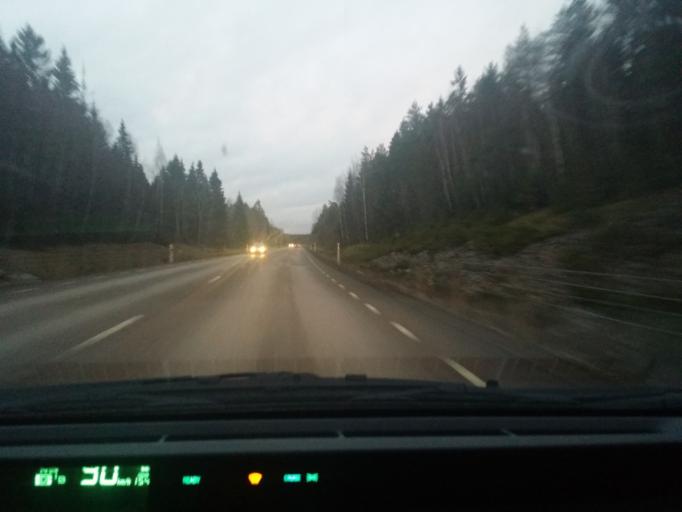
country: SE
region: Soedermanland
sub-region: Eskilstuna Kommun
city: Kvicksund
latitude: 59.5075
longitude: 16.3083
